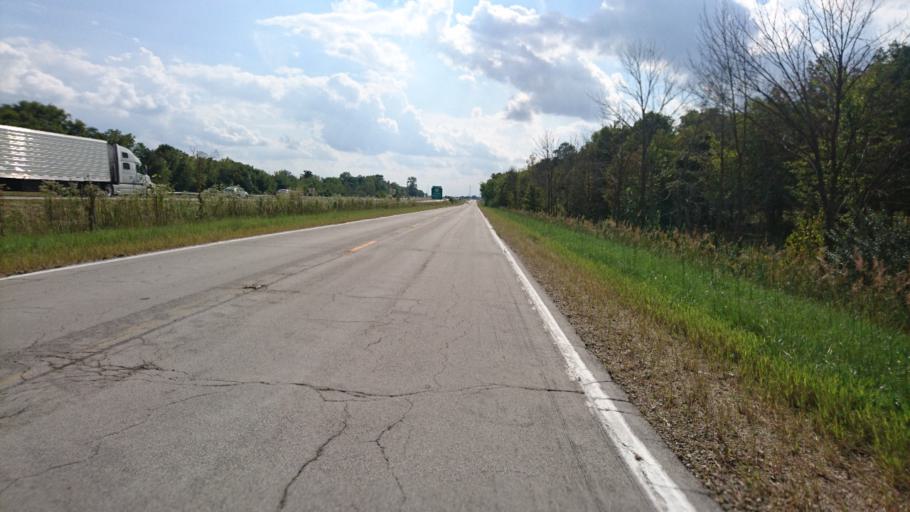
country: US
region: Illinois
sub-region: Logan County
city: Atlanta
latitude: 40.3423
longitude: -89.1369
